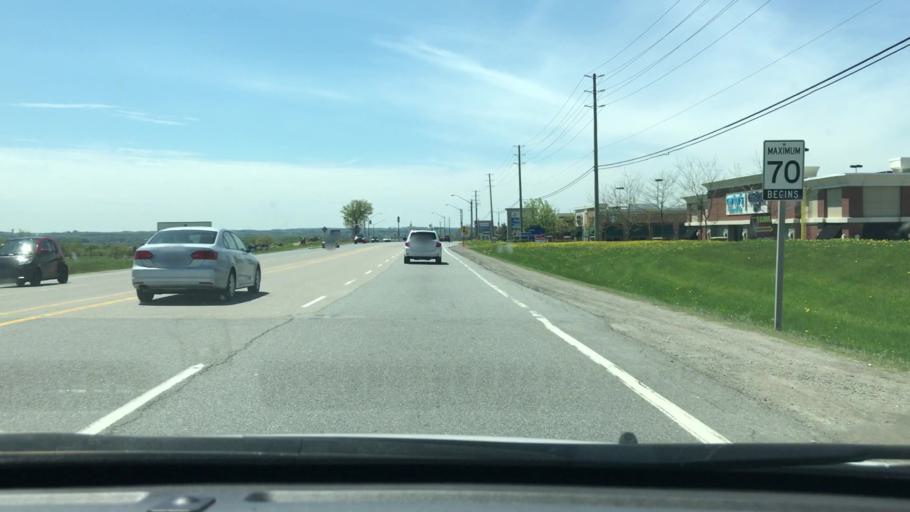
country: CA
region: Ontario
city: Newmarket
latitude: 44.0127
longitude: -79.4114
